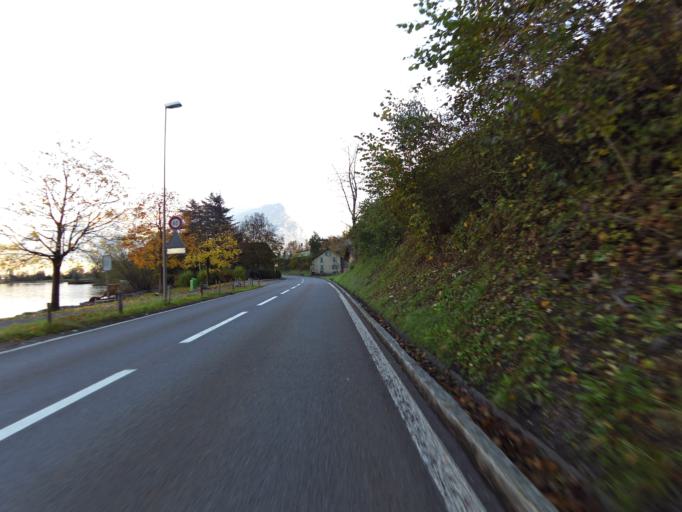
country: CH
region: Uri
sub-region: Uri
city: Seedorf
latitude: 46.8899
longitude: 8.5983
